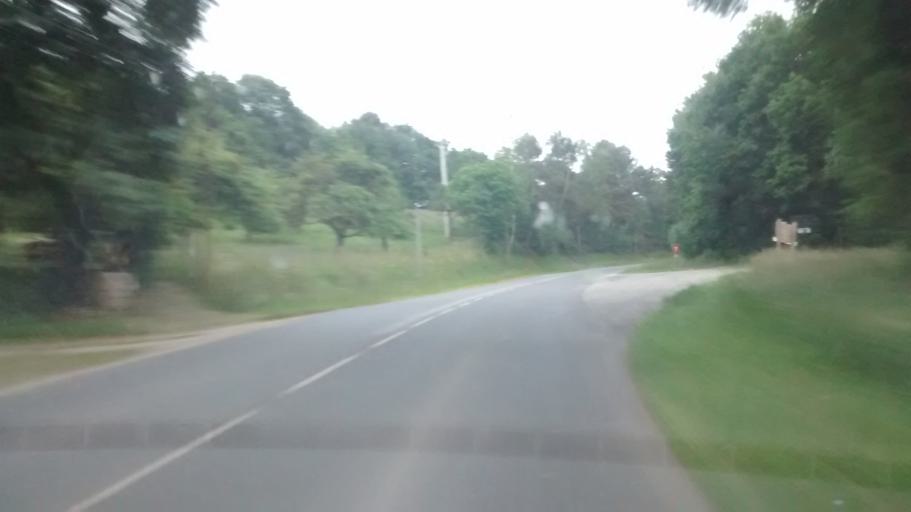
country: FR
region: Brittany
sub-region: Departement du Morbihan
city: Saint-Martin-sur-Oust
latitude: 47.7380
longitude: -2.2760
